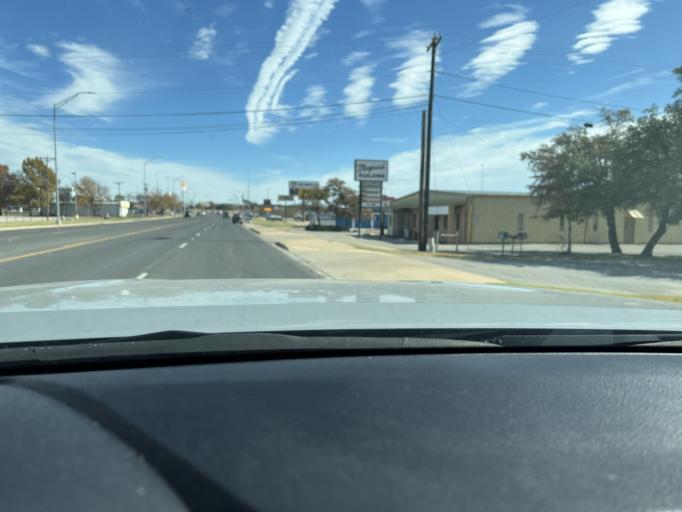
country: US
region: Texas
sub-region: Eastland County
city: Eastland
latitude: 32.4016
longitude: -98.7969
